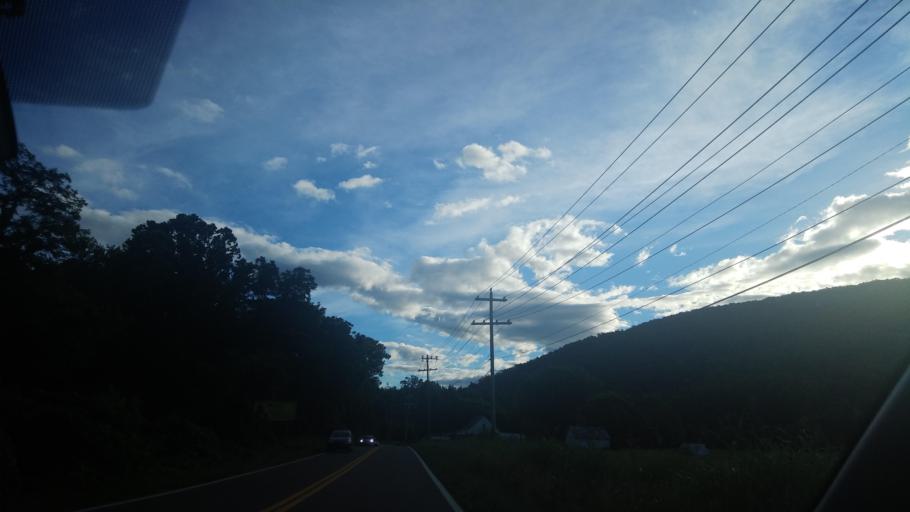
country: US
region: Tennessee
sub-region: Cocke County
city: Newport
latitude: 35.8100
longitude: -83.2487
